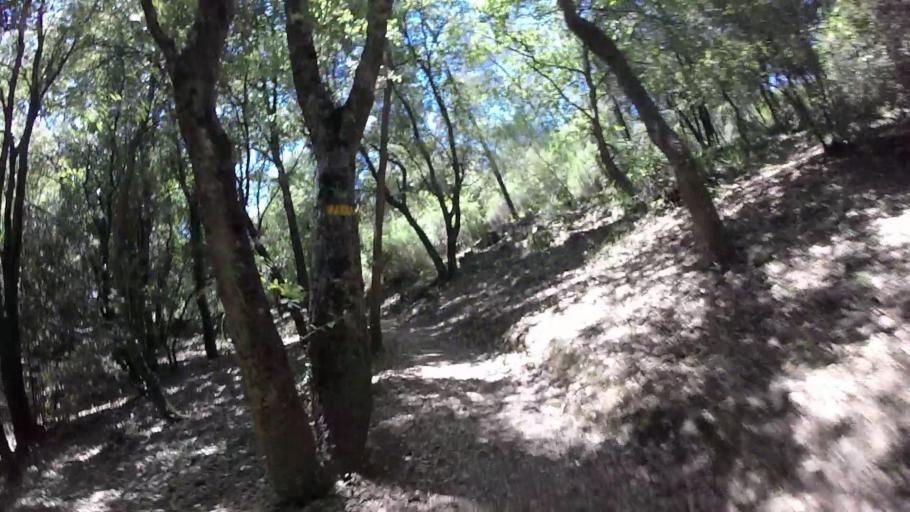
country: FR
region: Provence-Alpes-Cote d'Azur
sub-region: Departement des Alpes-Maritimes
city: Vallauris
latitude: 43.6062
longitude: 7.0436
